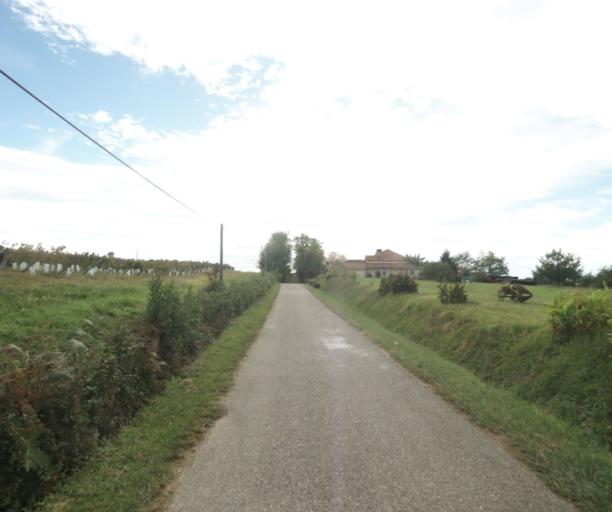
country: FR
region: Aquitaine
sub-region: Departement des Landes
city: Villeneuve-de-Marsan
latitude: 43.8994
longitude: -0.1946
